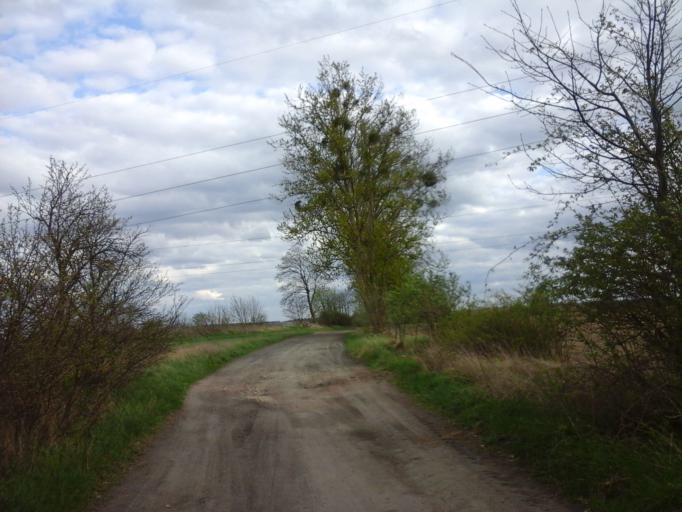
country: PL
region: West Pomeranian Voivodeship
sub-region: Powiat choszczenski
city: Krzecin
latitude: 53.0910
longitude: 15.5375
